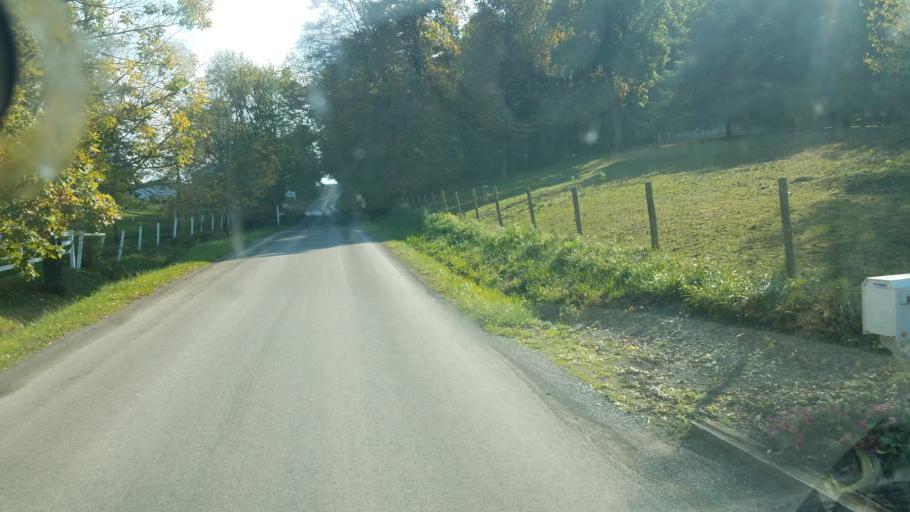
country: US
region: Ohio
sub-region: Wayne County
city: Apple Creek
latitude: 40.6683
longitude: -81.8420
